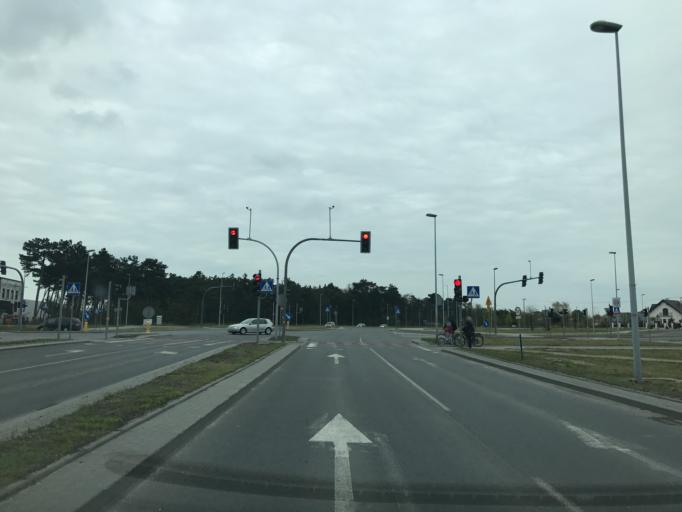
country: PL
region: Kujawsko-Pomorskie
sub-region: Torun
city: Torun
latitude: 53.0392
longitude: 18.5994
